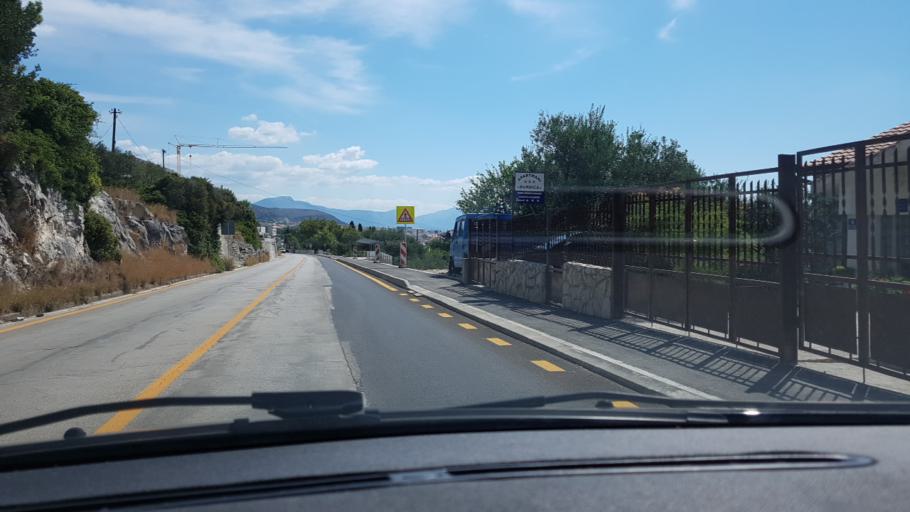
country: HR
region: Splitsko-Dalmatinska
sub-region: Grad Trogir
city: Trogir
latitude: 43.5169
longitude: 16.2165
